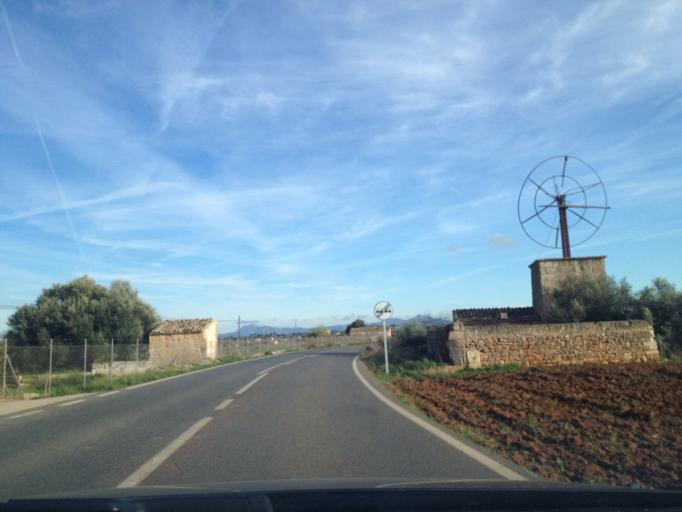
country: ES
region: Balearic Islands
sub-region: Illes Balears
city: Muro
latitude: 39.7655
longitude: 3.0992
